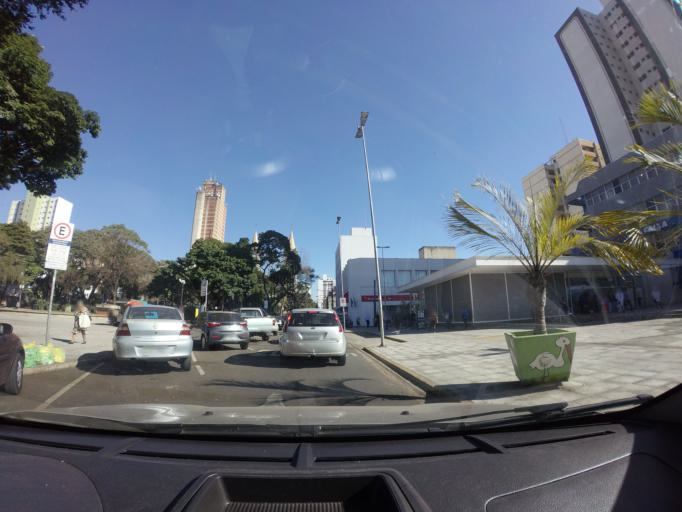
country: BR
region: Sao Paulo
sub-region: Piracicaba
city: Piracicaba
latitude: -22.7239
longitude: -47.6489
